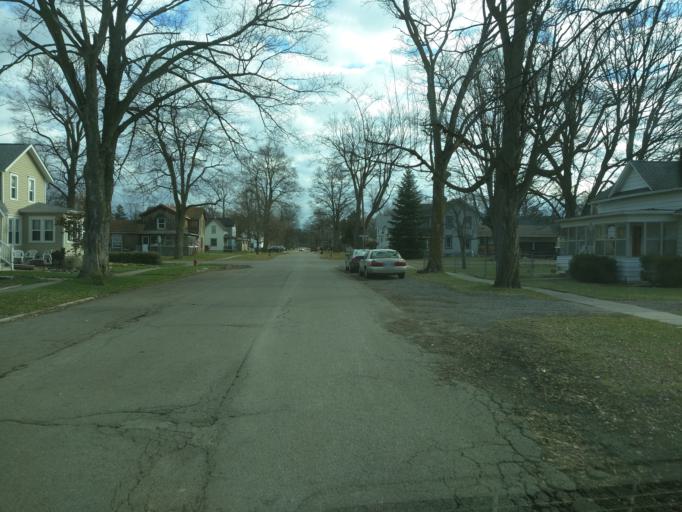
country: US
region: Michigan
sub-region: Livingston County
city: Fowlerville
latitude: 42.6596
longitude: -84.0713
